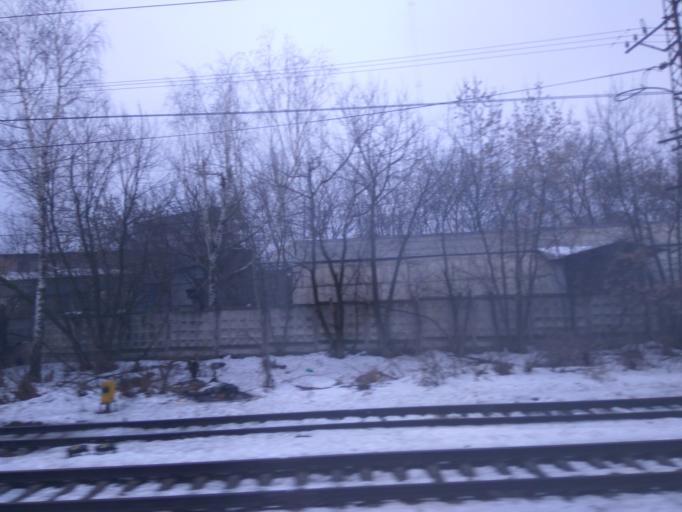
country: RU
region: Moscow
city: Mar'ina Roshcha
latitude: 55.8045
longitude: 37.6227
